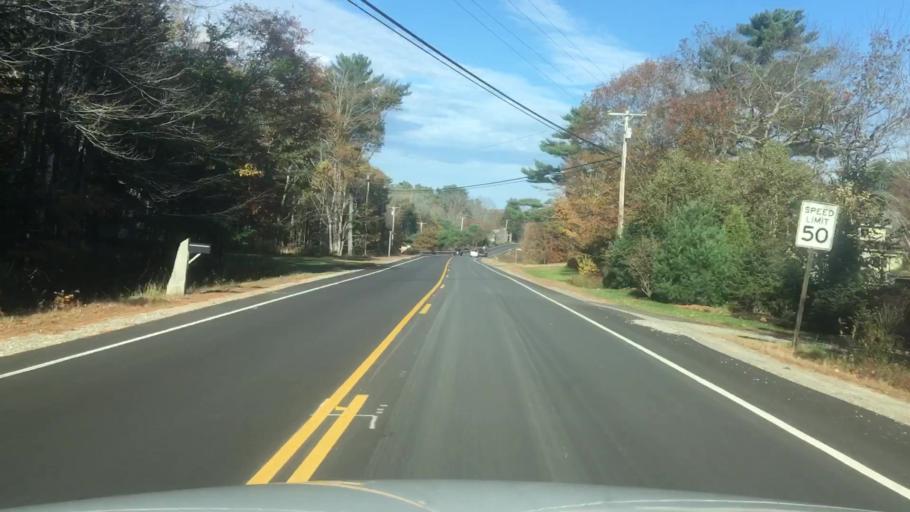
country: US
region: Maine
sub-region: Sagadahoc County
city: Woolwich
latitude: 43.8896
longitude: -69.7899
